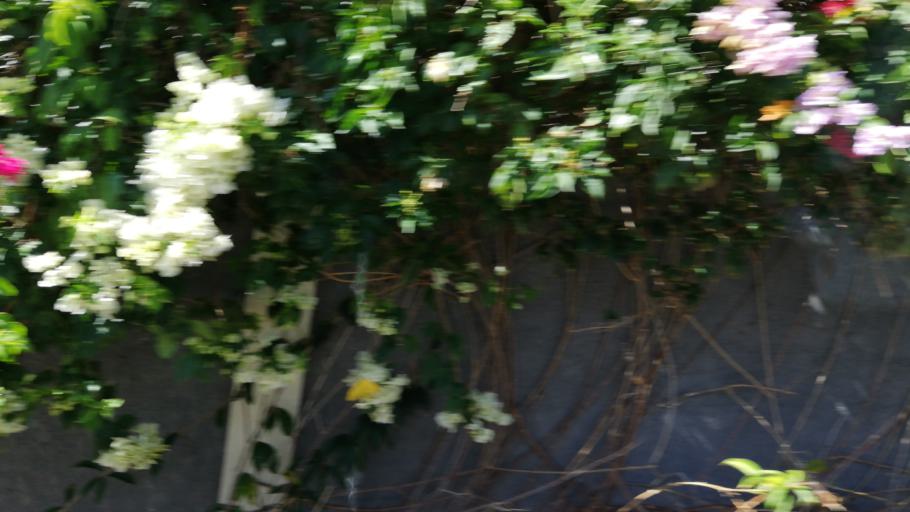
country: MU
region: Plaines Wilhems
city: Ebene
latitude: -20.2365
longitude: 57.4790
